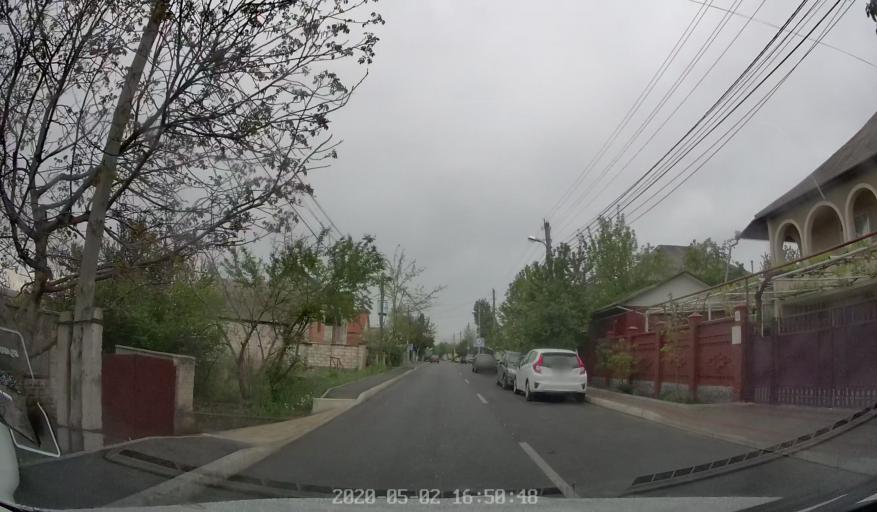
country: MD
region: Chisinau
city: Chisinau
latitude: 46.9651
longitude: 28.8299
